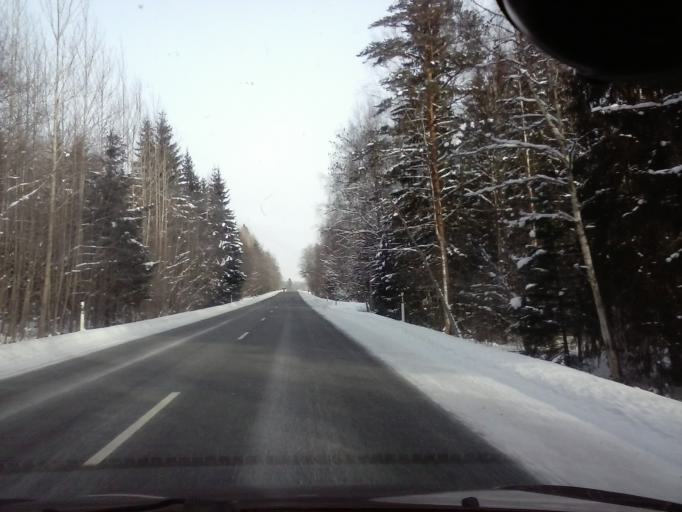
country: EE
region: Viljandimaa
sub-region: Abja vald
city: Abja-Paluoja
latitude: 58.2637
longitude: 25.2484
